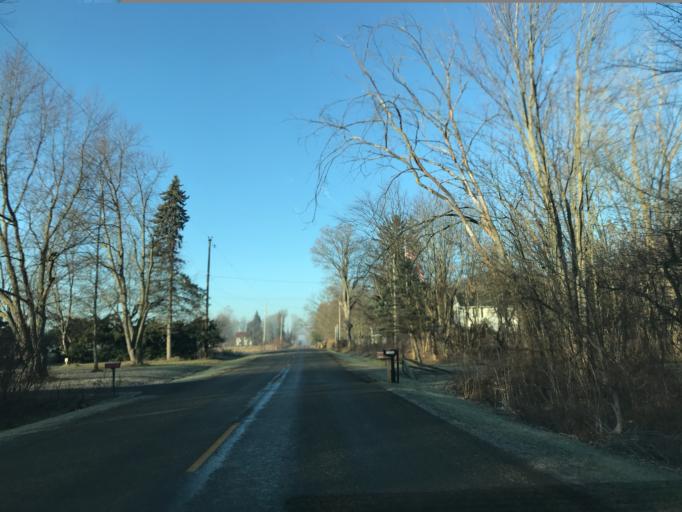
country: US
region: Michigan
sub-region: Eaton County
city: Dimondale
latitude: 42.6621
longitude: -84.6090
